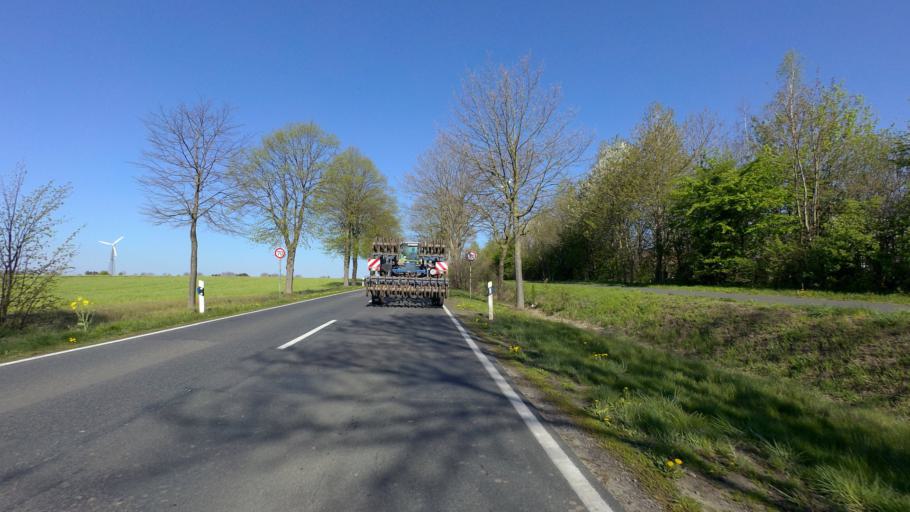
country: DE
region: Lower Saxony
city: Steimbke
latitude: 52.6526
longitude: 9.4067
